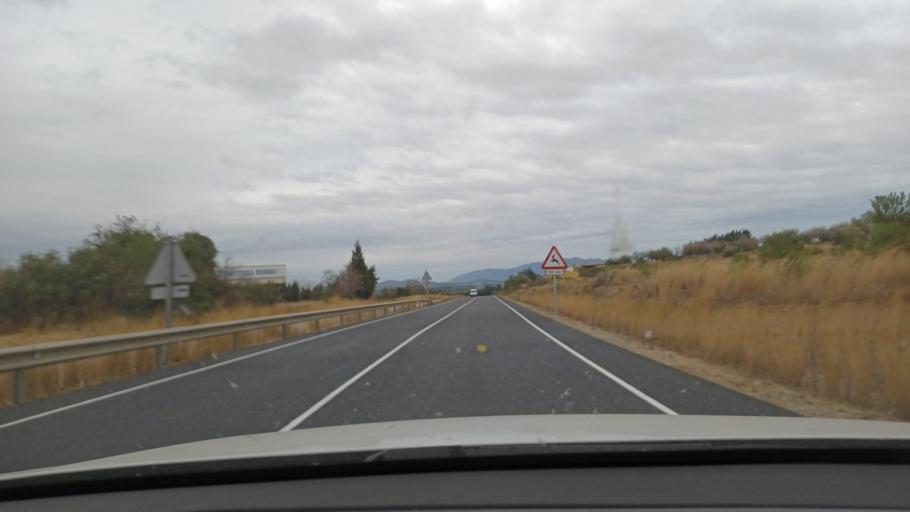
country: ES
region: Valencia
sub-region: Provincia de Castello
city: Traiguera
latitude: 40.5297
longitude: 0.2955
